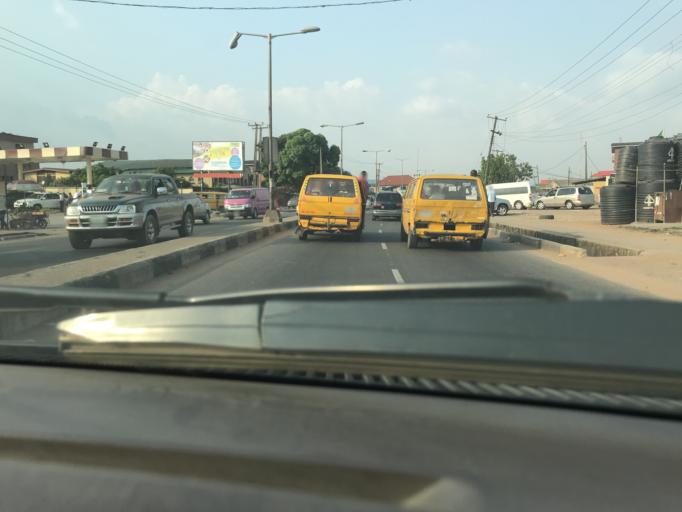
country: NG
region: Lagos
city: Agege
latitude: 6.5925
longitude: 3.2877
